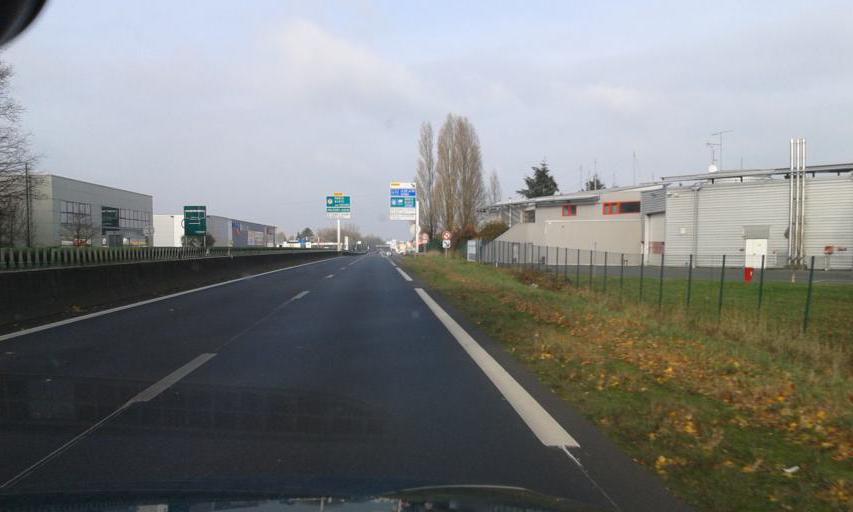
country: FR
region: Centre
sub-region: Departement du Loiret
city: Olivet
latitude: 47.8366
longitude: 1.9161
